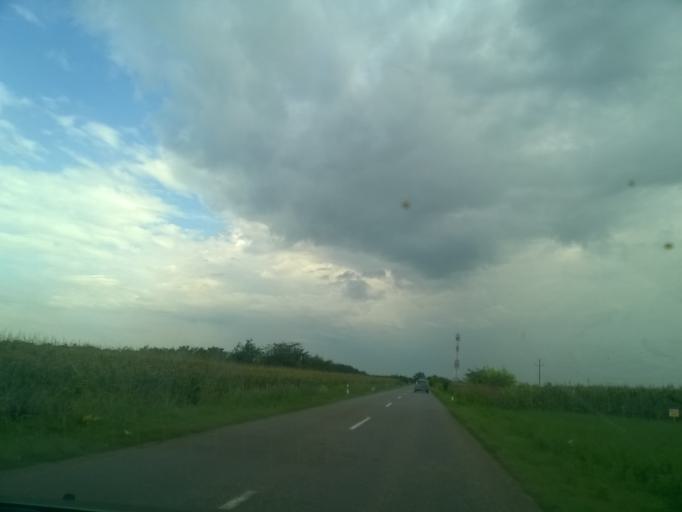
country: RS
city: Tomasevac
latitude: 45.2571
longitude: 20.6287
